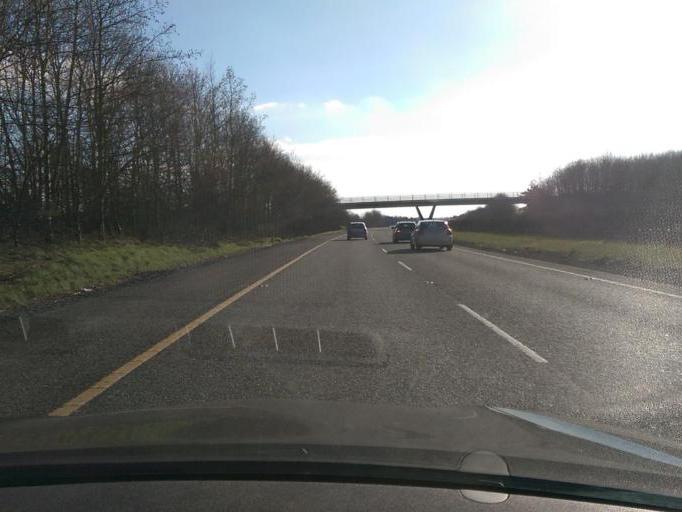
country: IE
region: Leinster
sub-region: Kildare
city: Naas
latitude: 53.1954
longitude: -6.7224
